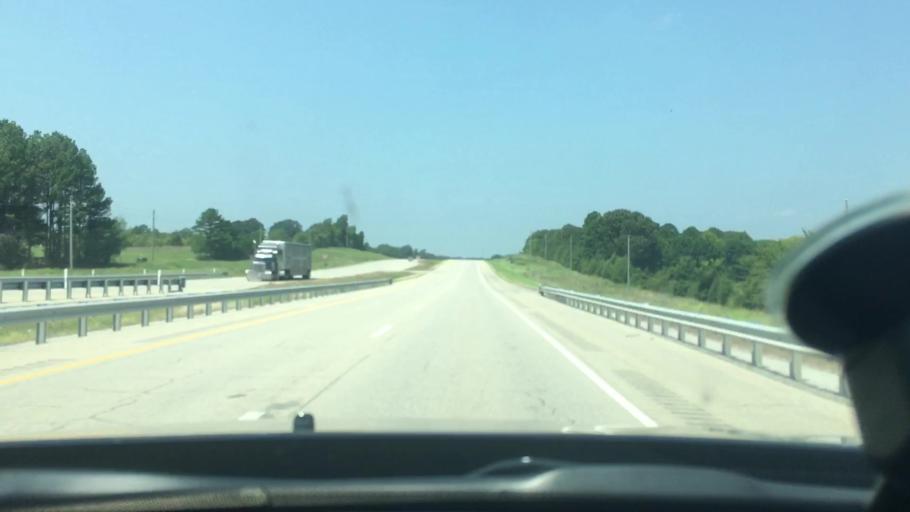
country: US
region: Oklahoma
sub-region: Atoka County
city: Atoka
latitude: 34.3098
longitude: -96.0145
